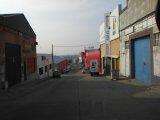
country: ES
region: Castille and Leon
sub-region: Provincia de Salamanca
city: Villares de la Reina
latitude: 40.9892
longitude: -5.6423
